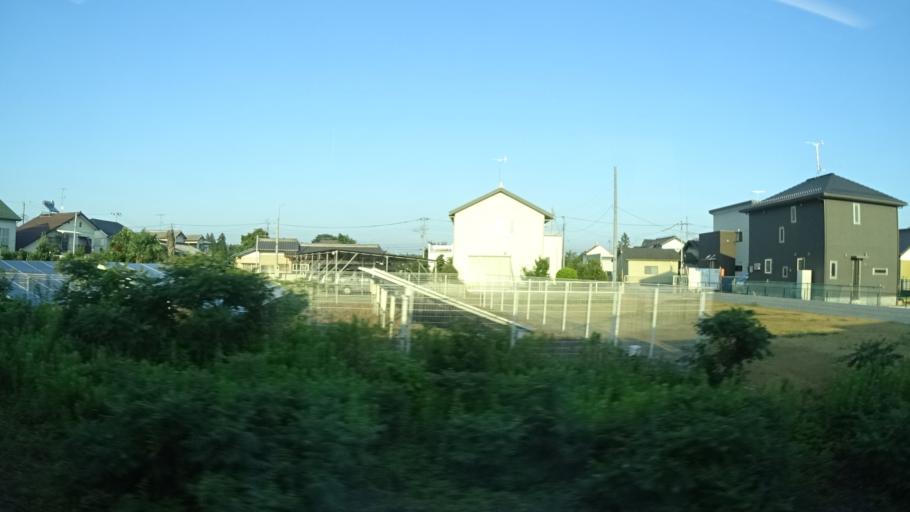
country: JP
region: Ibaraki
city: Ishioka
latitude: 36.2087
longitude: 140.2810
